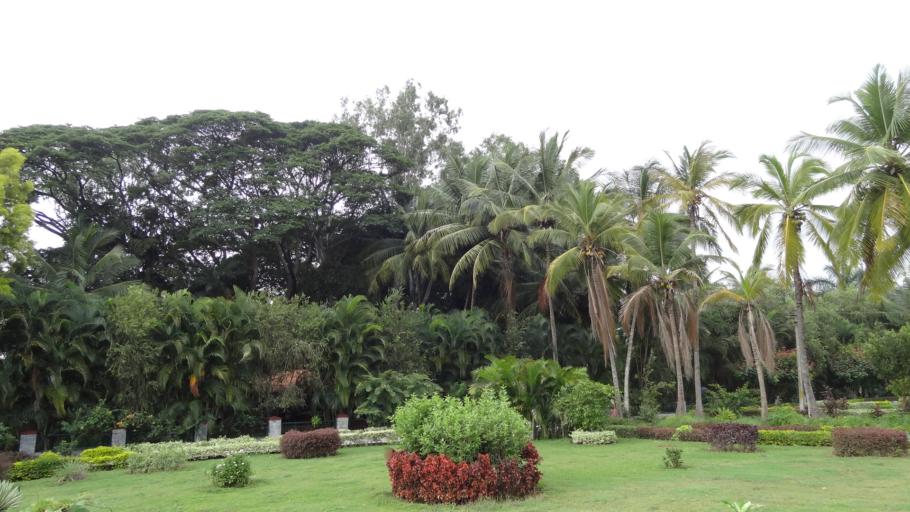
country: IN
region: Karnataka
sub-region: Mandya
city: Shrirangapattana
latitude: 12.4232
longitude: 76.6549
